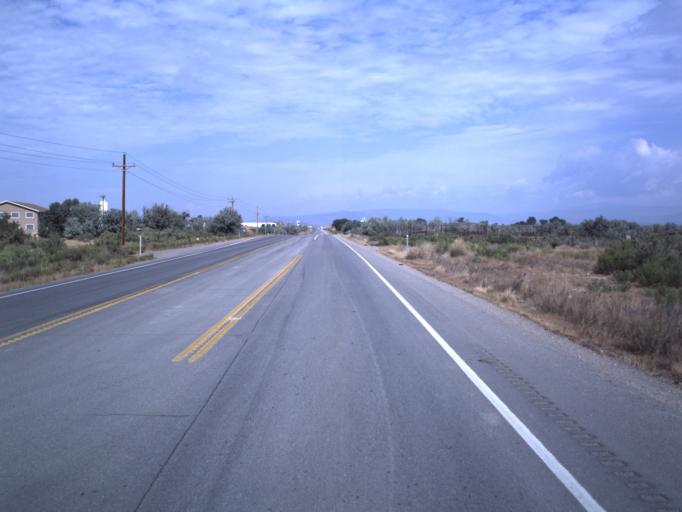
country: US
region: Utah
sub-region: Uintah County
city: Naples
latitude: 40.3822
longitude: -109.4246
